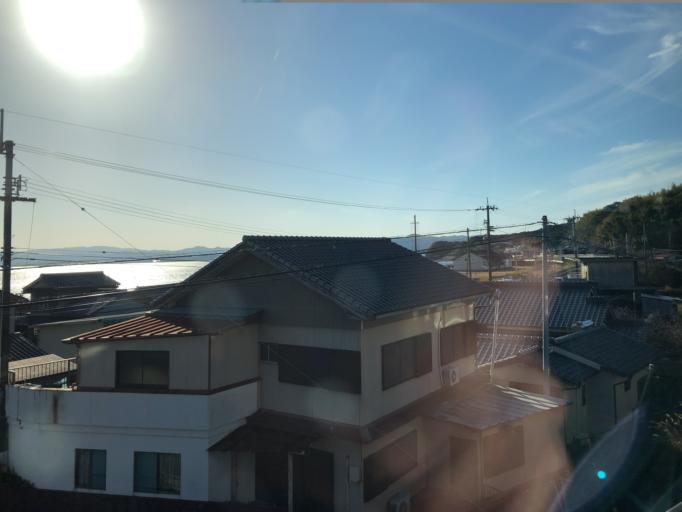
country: JP
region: Kochi
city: Nakamura
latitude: 33.0381
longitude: 133.0725
